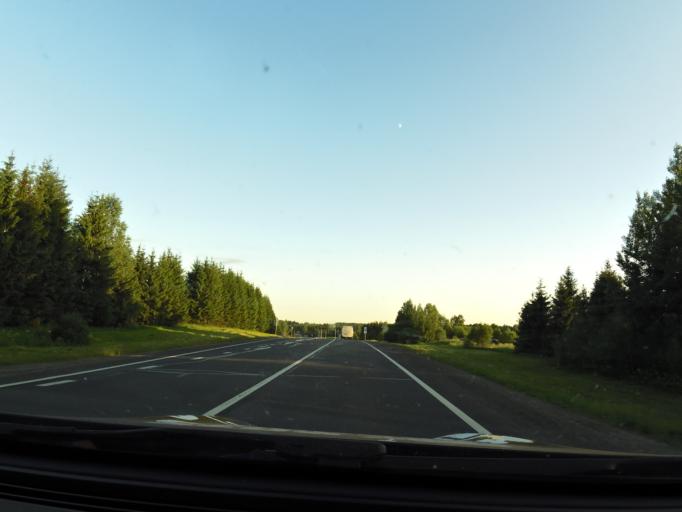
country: RU
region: Jaroslavl
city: Prechistoye
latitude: 58.4880
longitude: 40.3281
